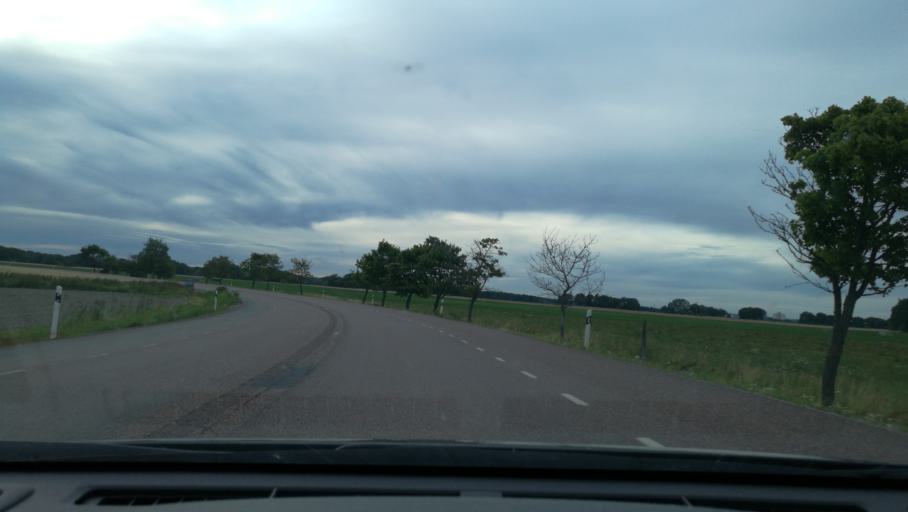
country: SE
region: Vaestmanland
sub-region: Kungsors Kommun
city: Kungsoer
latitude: 59.4332
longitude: 16.0829
